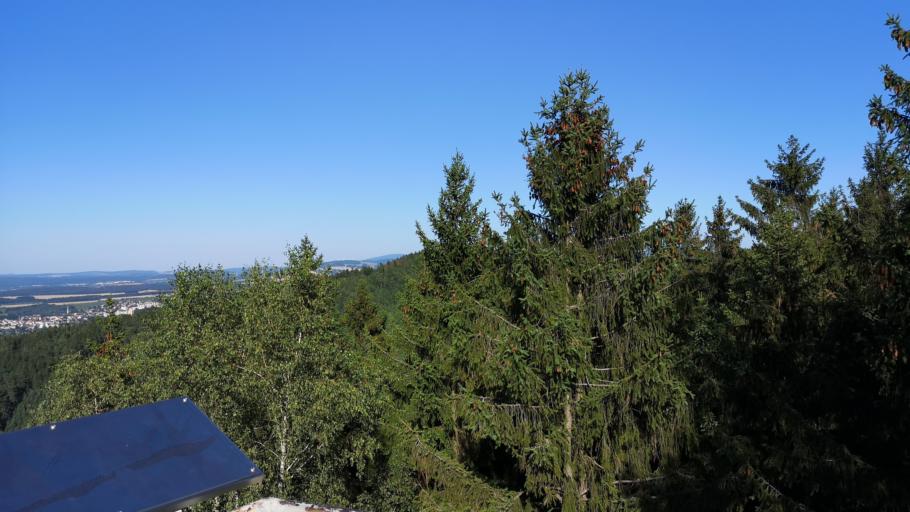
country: CZ
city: Hradek nad Nisou
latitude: 50.8314
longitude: 14.7959
